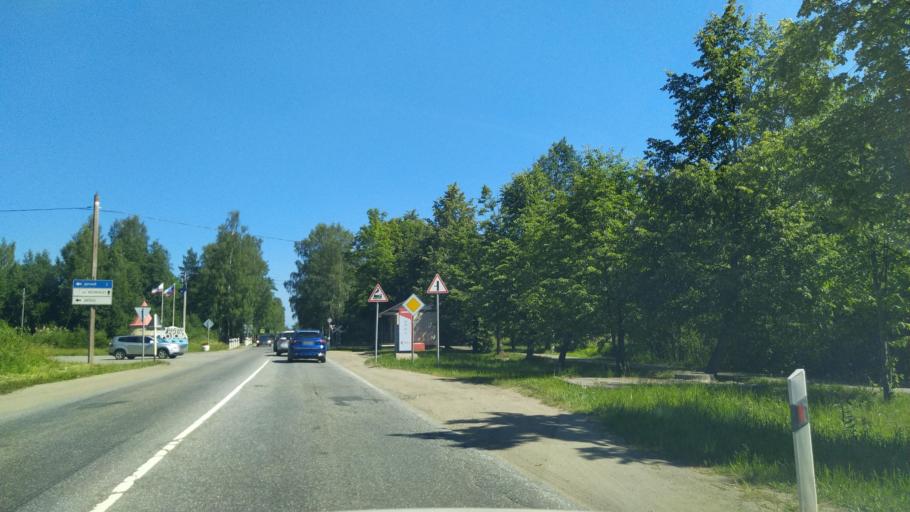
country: RU
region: Leningrad
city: Imeni Morozova
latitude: 59.9703
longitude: 31.0227
